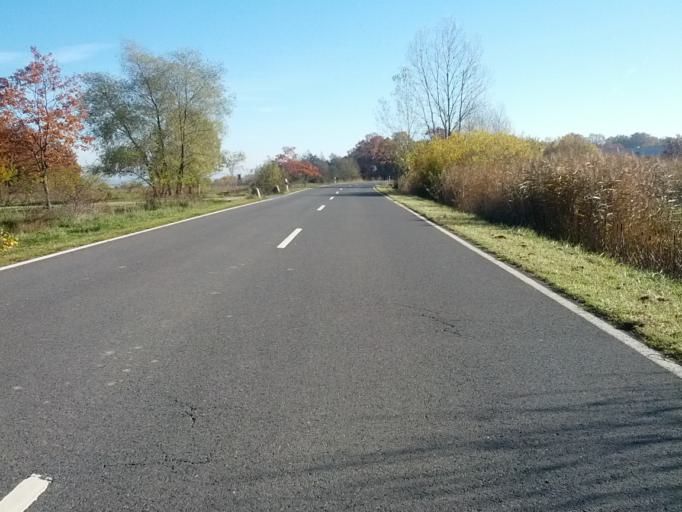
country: DE
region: Thuringia
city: Haina
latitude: 50.9985
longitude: 10.4660
